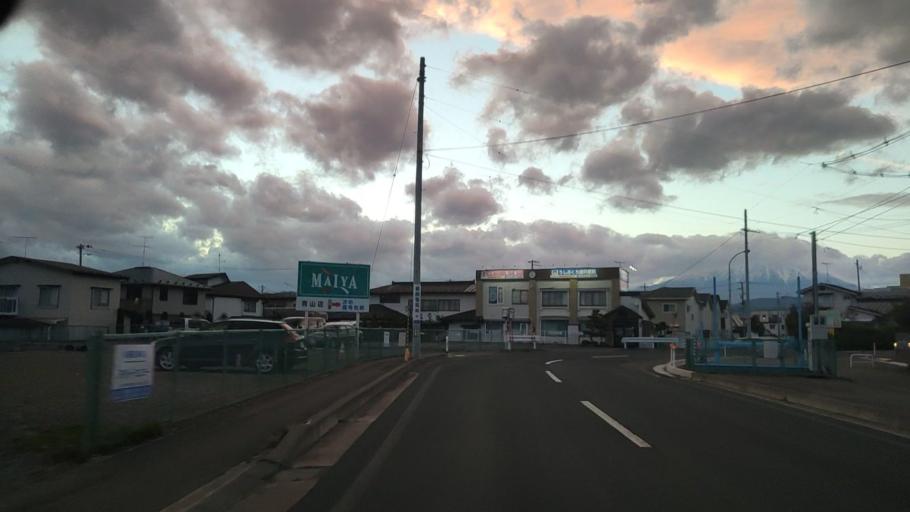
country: JP
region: Iwate
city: Morioka-shi
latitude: 39.7187
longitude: 141.1087
